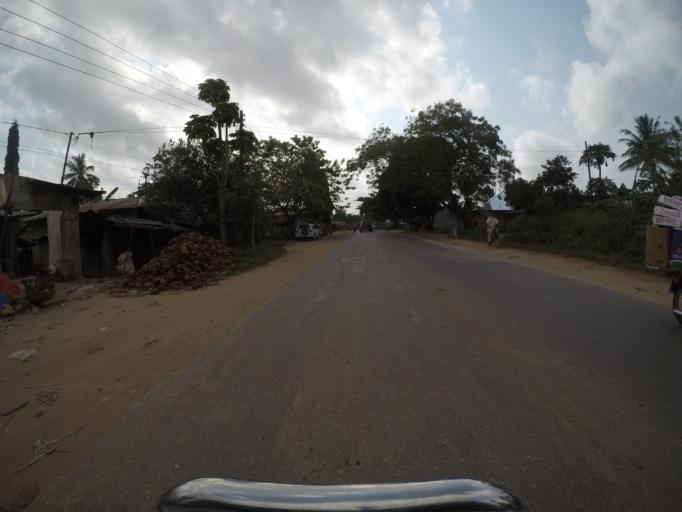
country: TZ
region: Zanzibar Central/South
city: Koani
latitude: -6.1958
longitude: 39.2787
